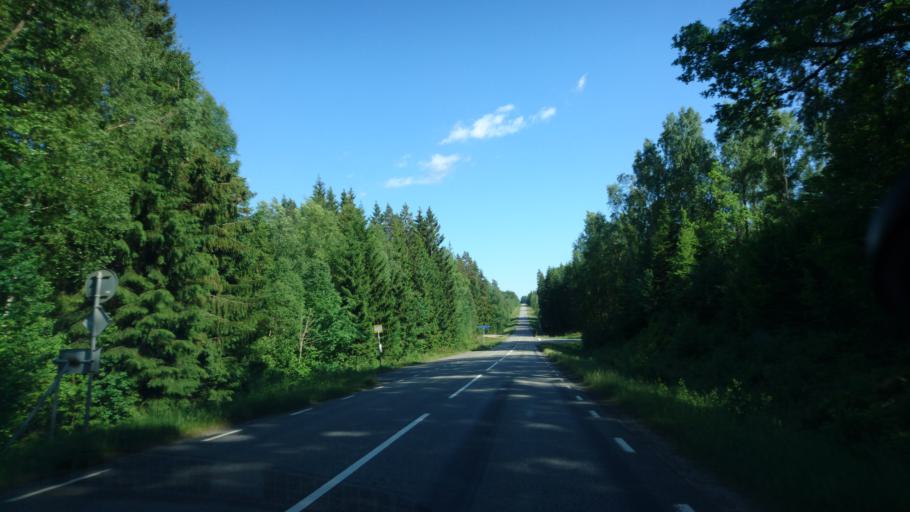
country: SE
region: Skane
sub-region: Osby Kommun
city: Lonsboda
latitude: 56.4432
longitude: 14.2412
